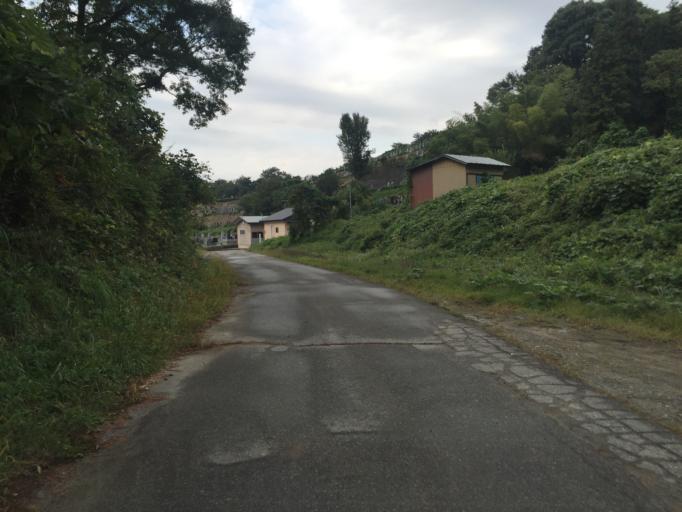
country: JP
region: Fukushima
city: Kitakata
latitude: 37.4804
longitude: 139.9483
